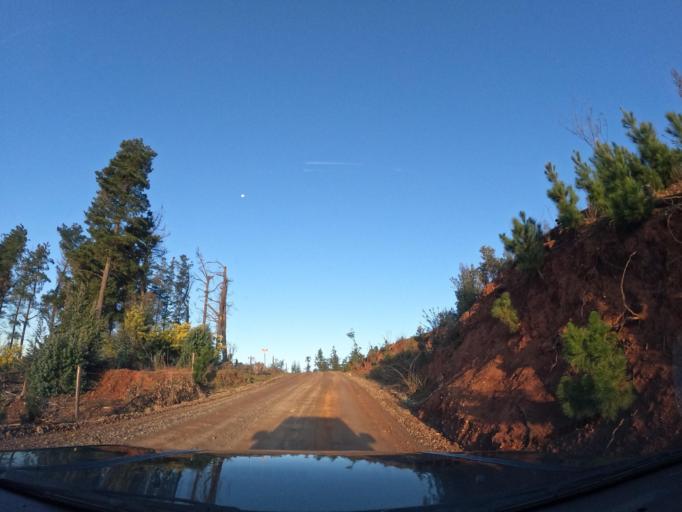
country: CL
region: Biobio
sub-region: Provincia de Concepcion
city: Chiguayante
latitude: -37.0105
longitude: -72.8871
